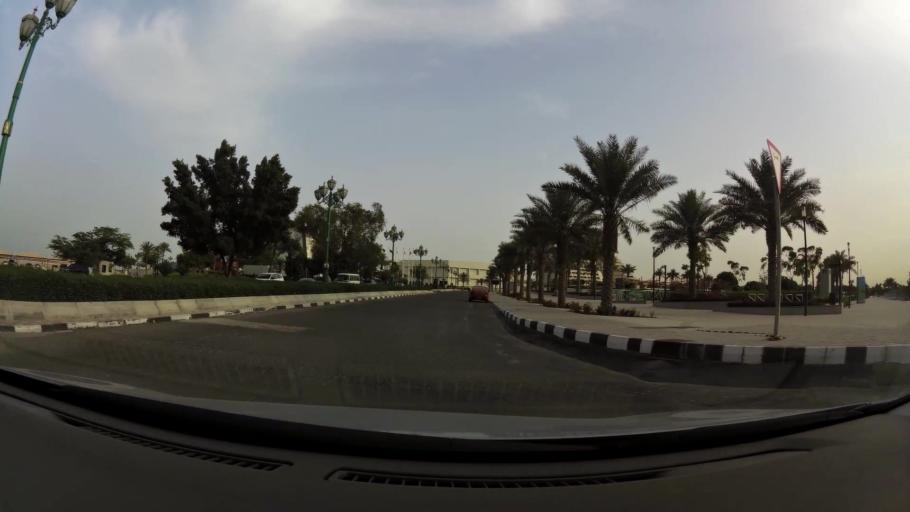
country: QA
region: Baladiyat ad Dawhah
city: Doha
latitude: 25.3224
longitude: 51.5363
